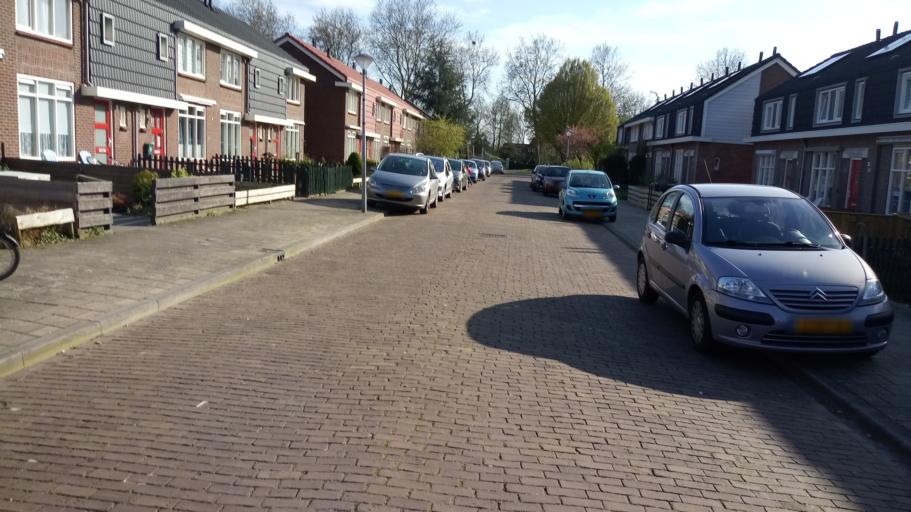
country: NL
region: Gelderland
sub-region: Gemeente Zutphen
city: Zutphen
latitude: 52.1316
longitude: 6.2046
